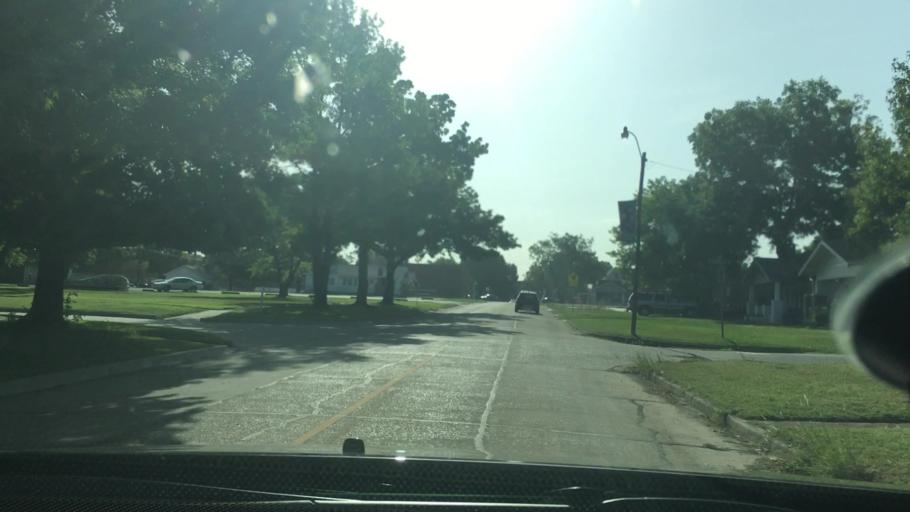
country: US
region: Oklahoma
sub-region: Pontotoc County
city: Ada
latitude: 34.7734
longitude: -96.6688
